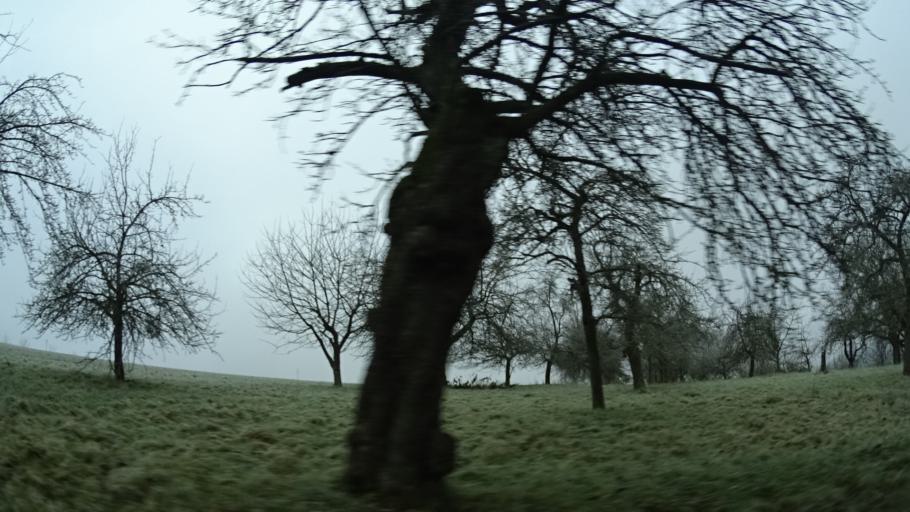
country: DE
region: Baden-Wuerttemberg
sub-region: Karlsruhe Region
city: Seckach
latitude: 49.4722
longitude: 9.3121
